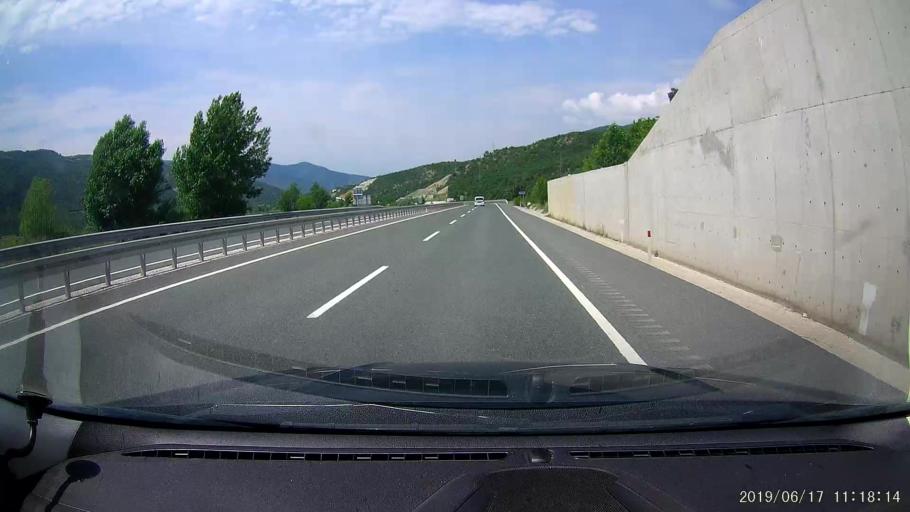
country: TR
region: Cankiri
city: Yaprakli
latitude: 40.9373
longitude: 33.8546
